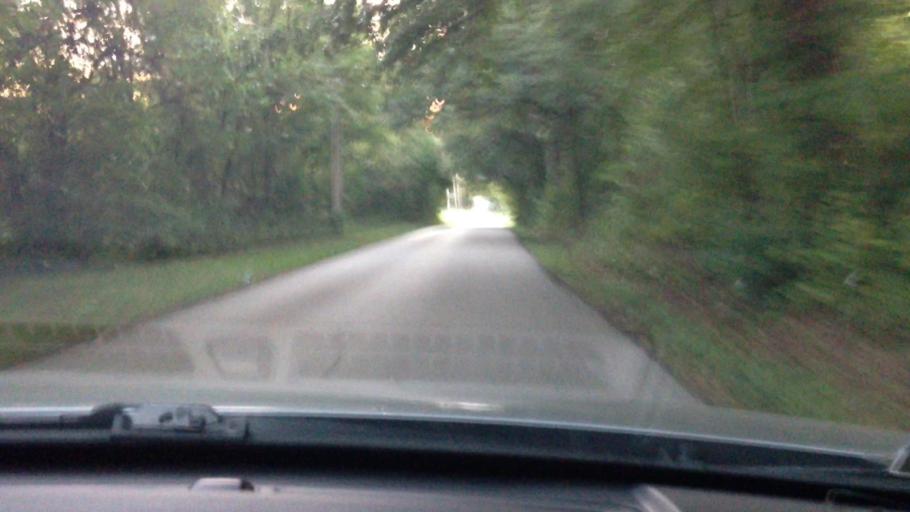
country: US
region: Kansas
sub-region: Leavenworth County
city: Lansing
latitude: 39.1795
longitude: -94.8345
